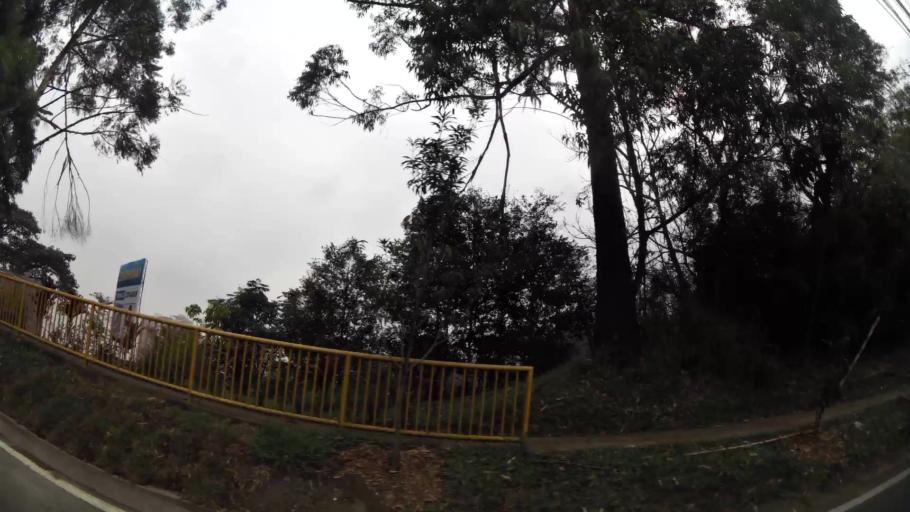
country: CO
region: Antioquia
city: Envigado
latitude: 6.1842
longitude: -75.5629
